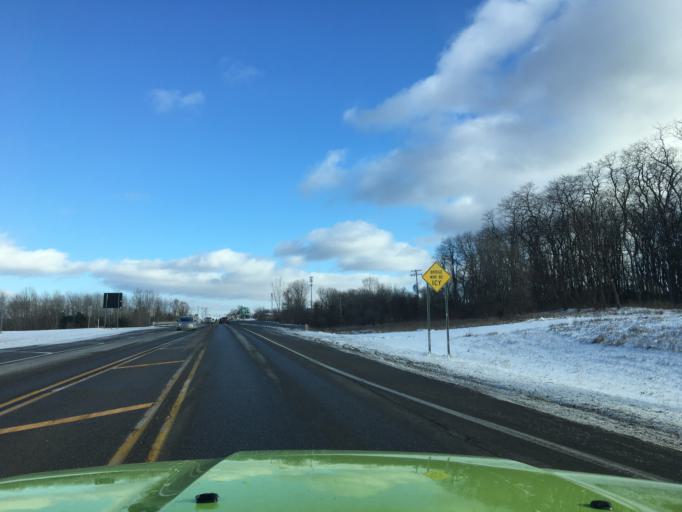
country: US
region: Michigan
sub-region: Kent County
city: Rockford
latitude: 43.1169
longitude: -85.6094
